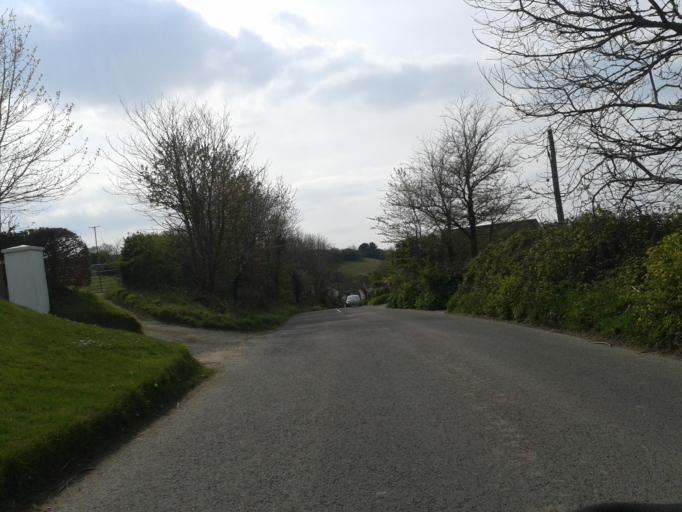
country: GB
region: England
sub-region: Devon
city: Braunton
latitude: 51.1307
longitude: -4.2114
